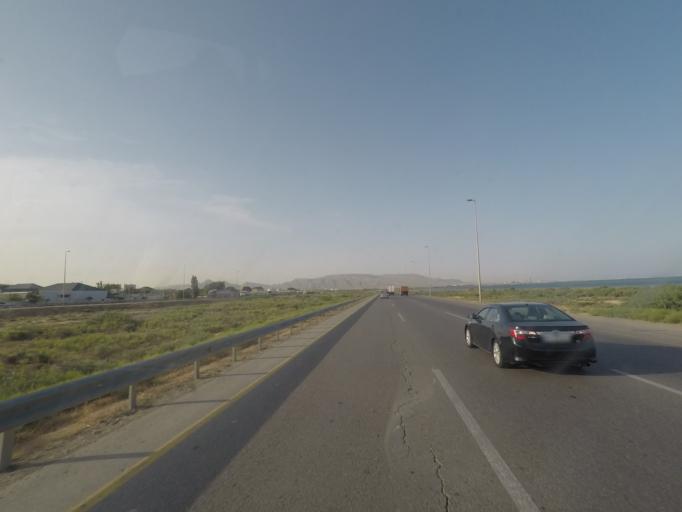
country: AZ
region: Baki
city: Qobustan
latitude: 40.1674
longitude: 49.4688
